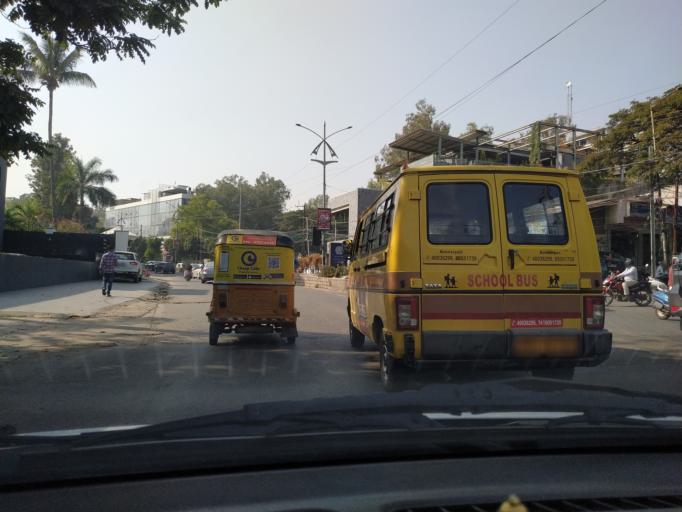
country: IN
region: Telangana
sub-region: Rangareddi
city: Kukatpalli
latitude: 17.4353
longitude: 78.4121
